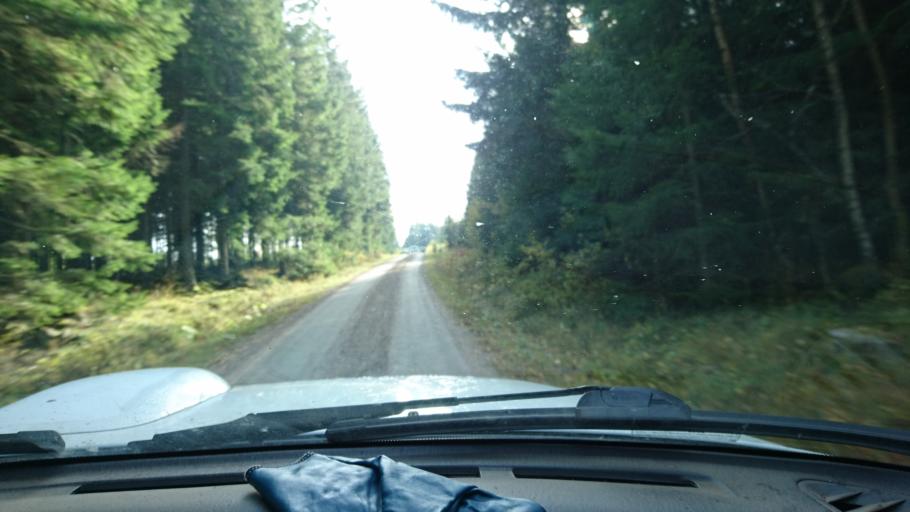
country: SE
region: Vaestra Goetaland
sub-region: Ulricehamns Kommun
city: Ulricehamn
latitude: 57.9487
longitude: 13.5352
